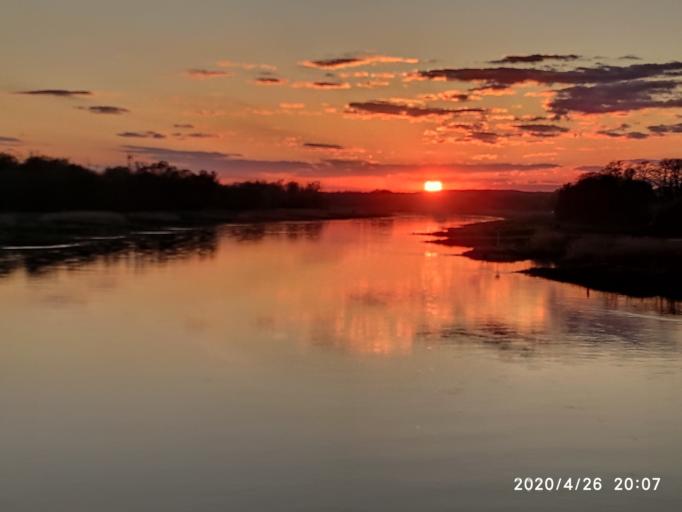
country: PL
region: Lubusz
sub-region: Powiat zielonogorski
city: Sulechow
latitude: 52.0299
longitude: 15.6139
